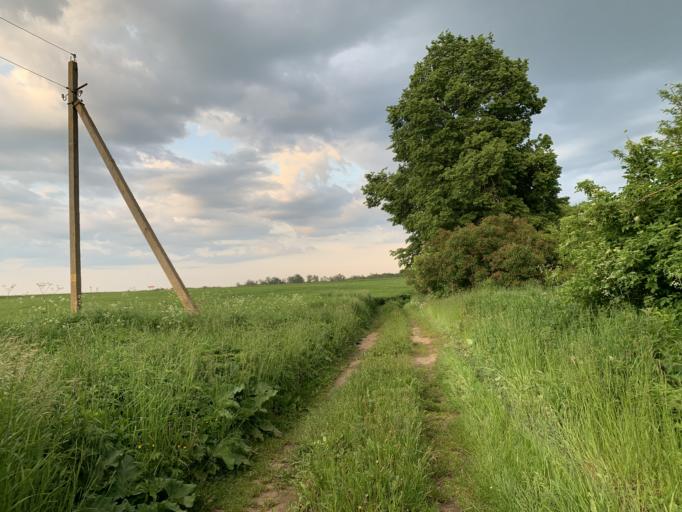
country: BY
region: Minsk
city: Nyasvizh
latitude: 53.1666
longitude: 26.8232
